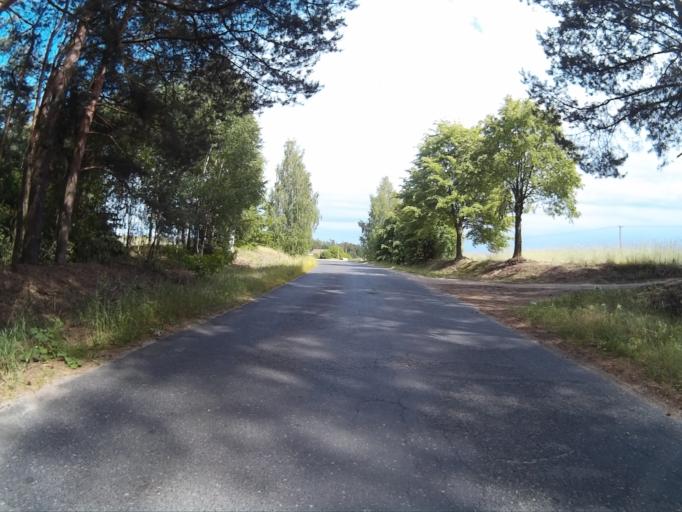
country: PL
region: Kujawsko-Pomorskie
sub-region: Powiat tucholski
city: Lubiewo
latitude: 53.4783
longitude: 17.9554
